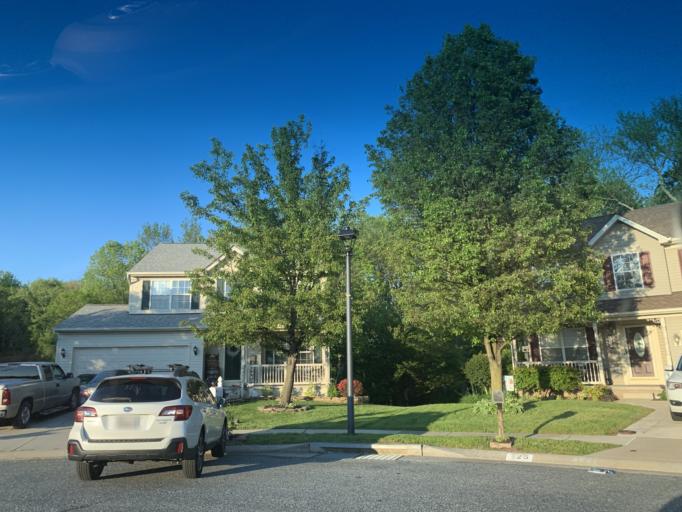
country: US
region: Maryland
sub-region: Harford County
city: Aberdeen
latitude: 39.5118
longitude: -76.1881
